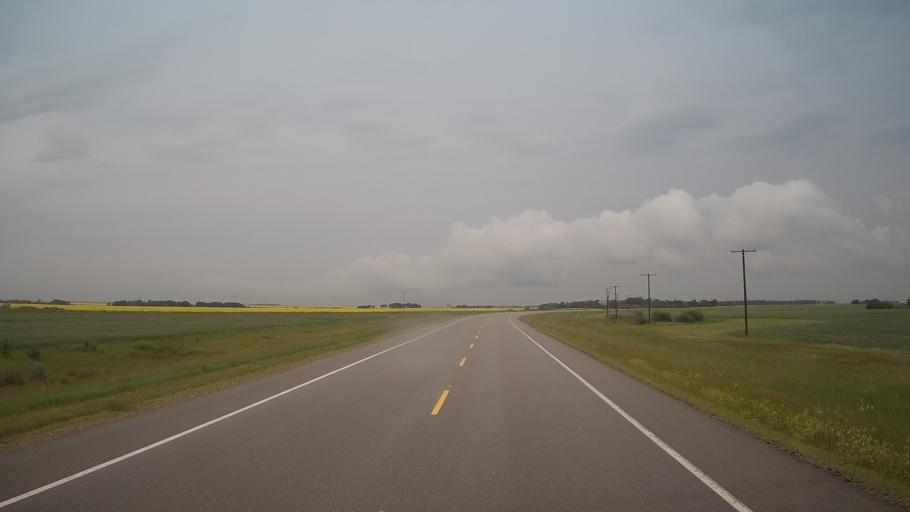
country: CA
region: Saskatchewan
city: Wilkie
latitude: 52.3282
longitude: -108.7102
